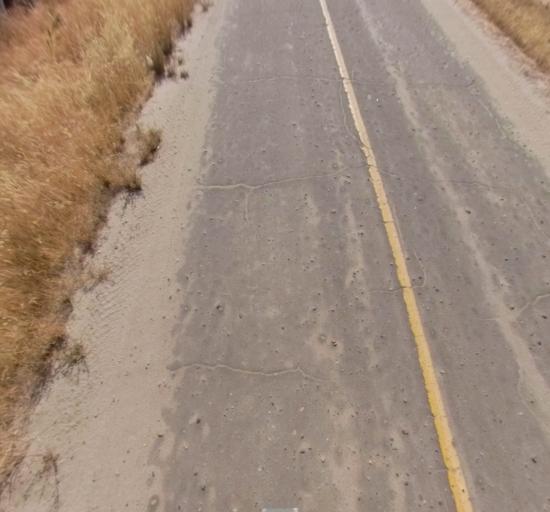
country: US
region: California
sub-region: Madera County
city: Fairmead
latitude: 37.0939
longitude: -120.2185
